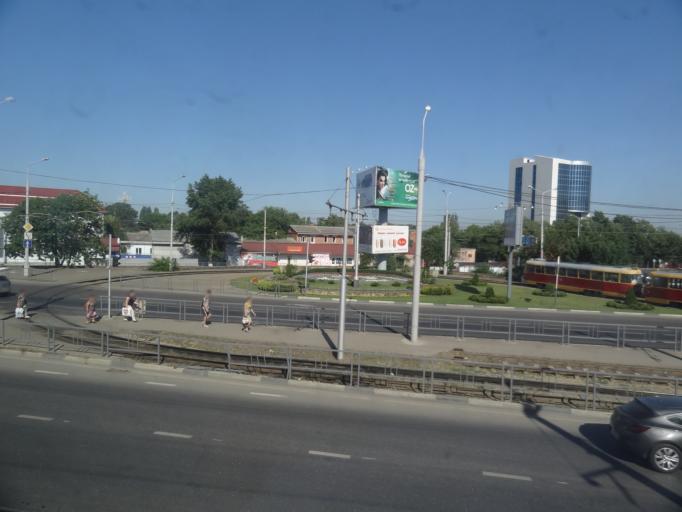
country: RU
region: Adygeya
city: Yablonovskiy
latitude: 44.9992
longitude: 38.9623
